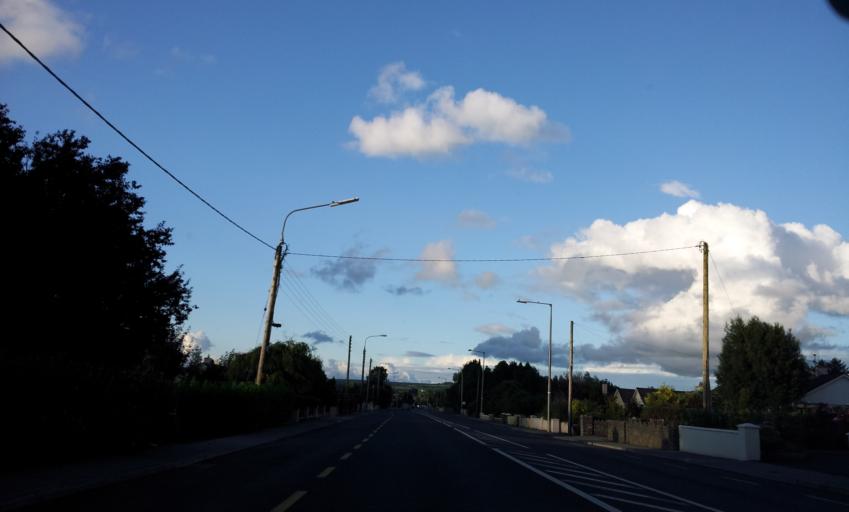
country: IE
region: Munster
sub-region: County Limerick
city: Abbeyfeale
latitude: 52.3753
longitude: -9.3091
